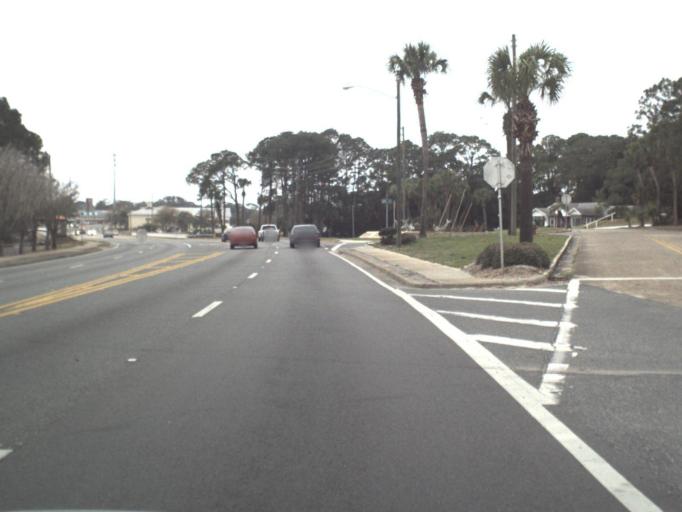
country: US
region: Florida
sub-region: Bay County
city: Panama City
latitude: 30.1573
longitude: -85.6412
